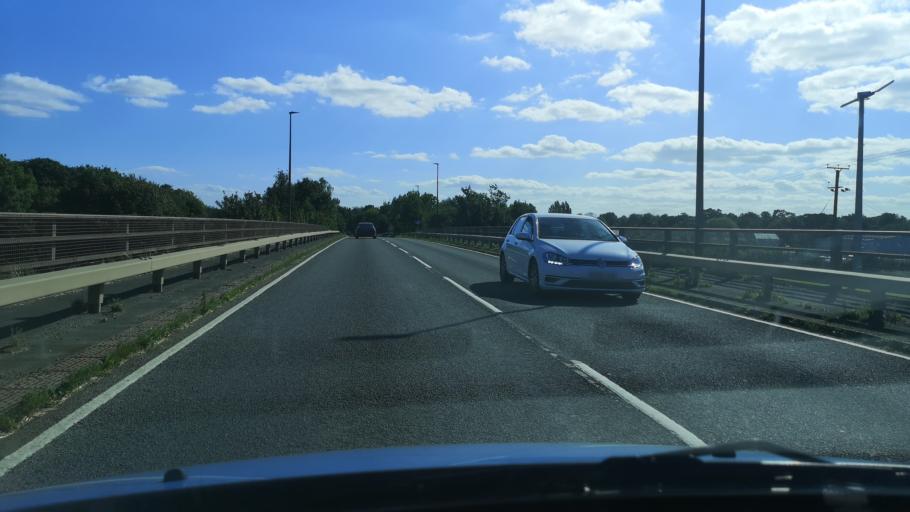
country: GB
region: England
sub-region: North Lincolnshire
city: Crowle
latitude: 53.5904
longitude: -0.8189
